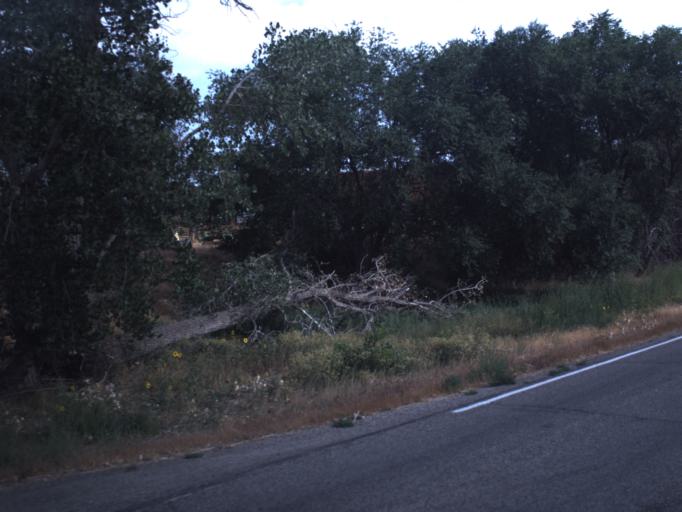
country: US
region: Utah
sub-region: Uintah County
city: Naples
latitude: 40.4036
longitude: -109.3436
